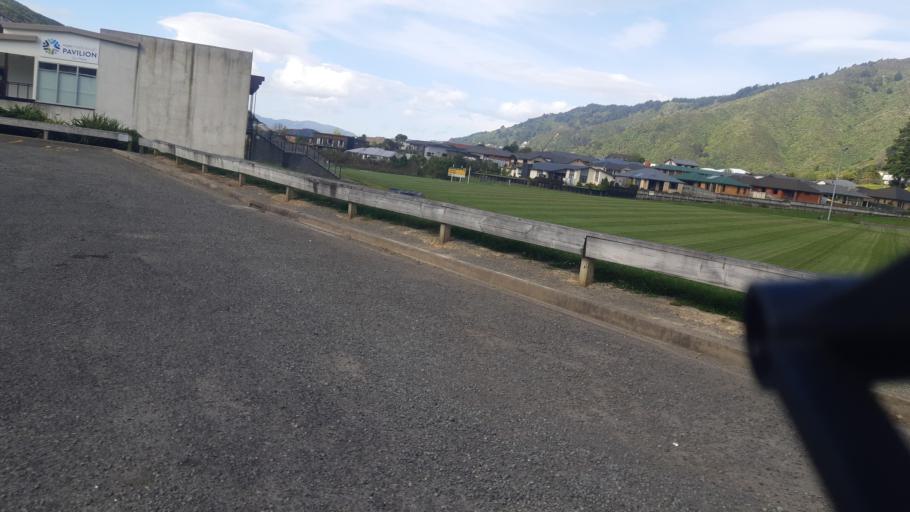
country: NZ
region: Marlborough
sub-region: Marlborough District
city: Picton
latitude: -41.2773
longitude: 174.0234
